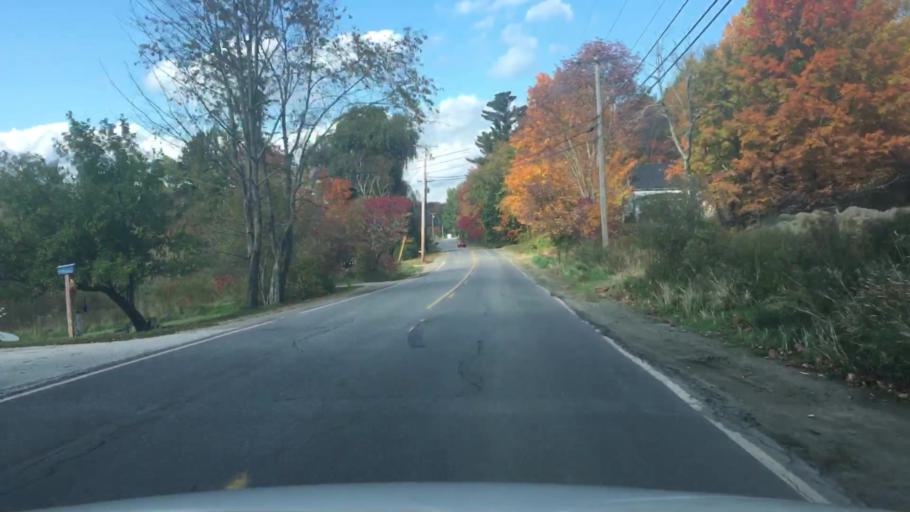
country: US
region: Maine
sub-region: Knox County
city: Union
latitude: 44.2076
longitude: -69.2622
